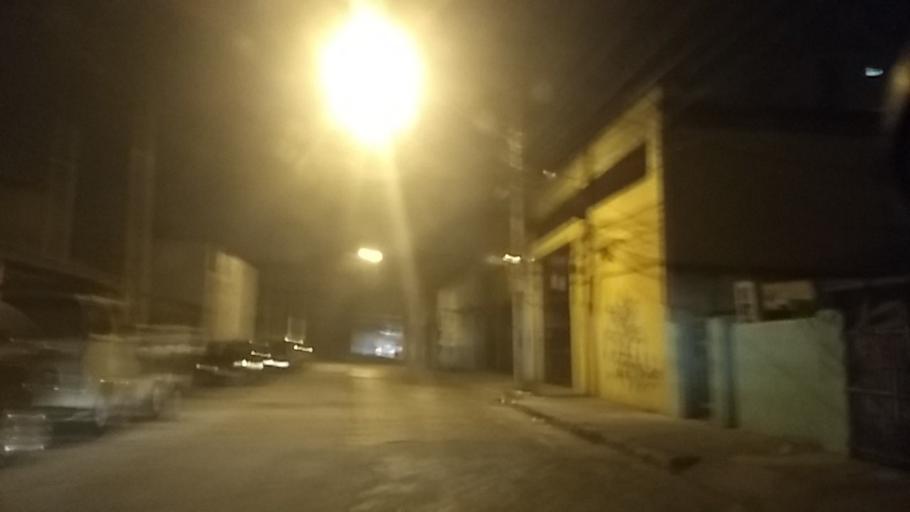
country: BR
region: Sao Paulo
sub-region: Sao Paulo
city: Sao Paulo
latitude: -23.5354
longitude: -46.6009
